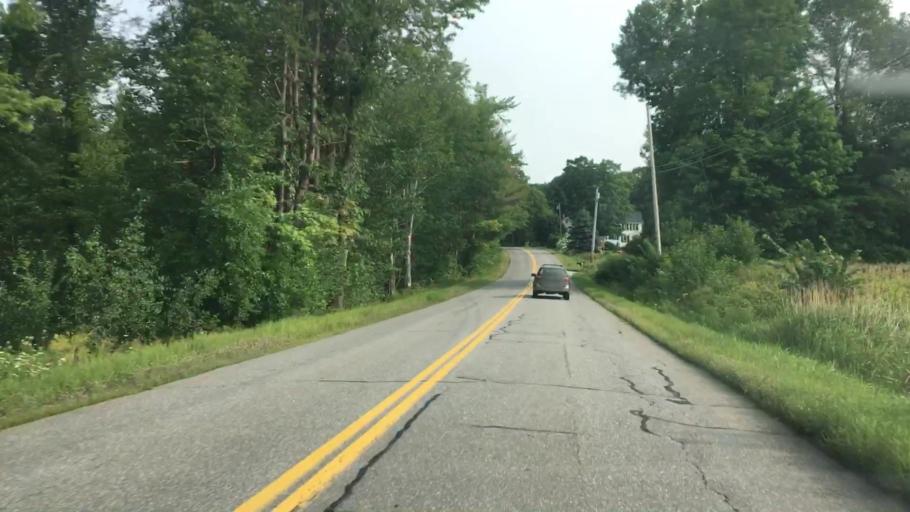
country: US
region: Maine
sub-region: Kennebec County
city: Chelsea
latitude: 44.2944
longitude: -69.6976
